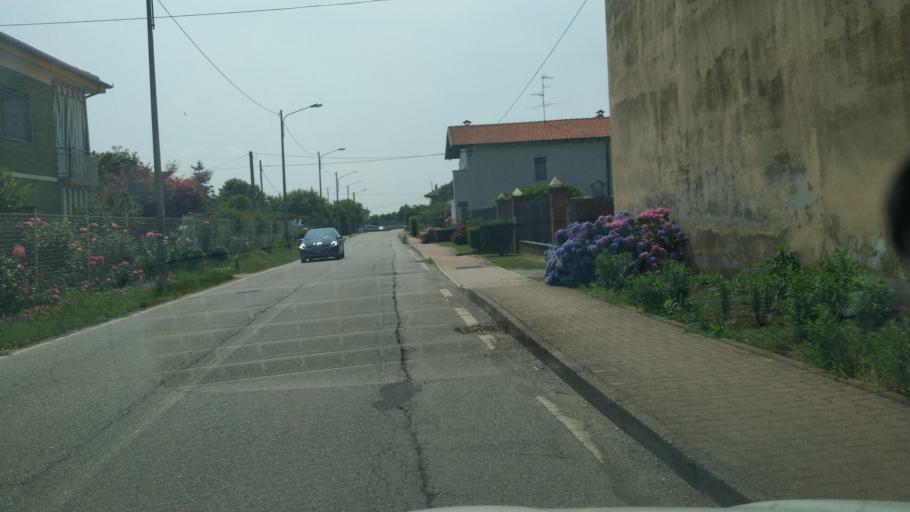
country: IT
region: Piedmont
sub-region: Provincia di Torino
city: Rondissone
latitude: 45.2432
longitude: 7.9701
